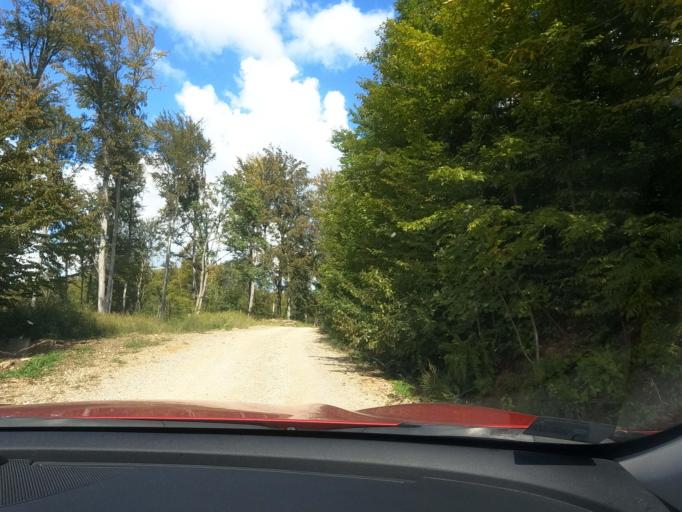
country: HR
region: Karlovacka
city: Vojnic
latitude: 45.2819
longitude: 15.7817
